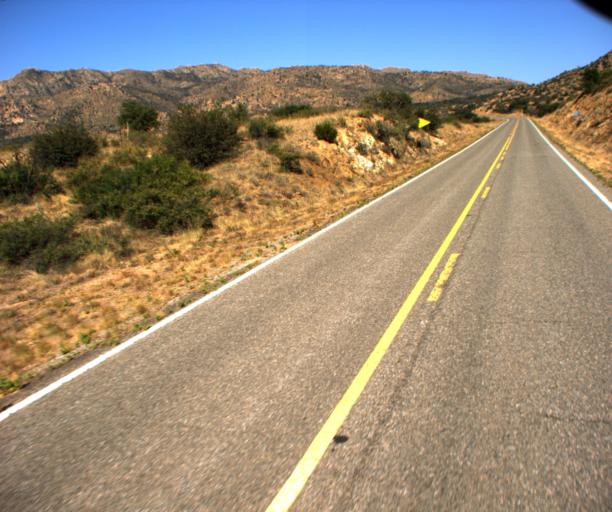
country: US
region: Arizona
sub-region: Graham County
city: Swift Trail Junction
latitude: 32.5707
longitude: -109.8151
